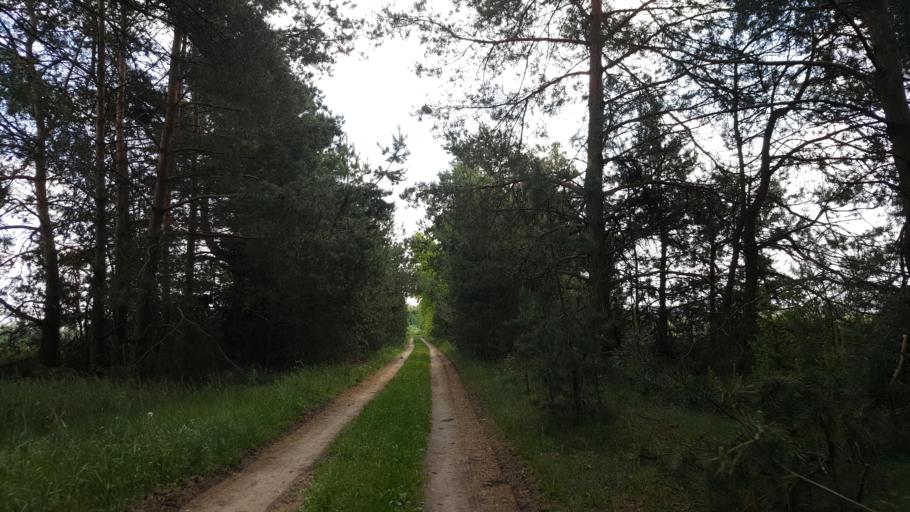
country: BY
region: Brest
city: Kamyanyets
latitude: 52.3920
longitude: 23.8752
